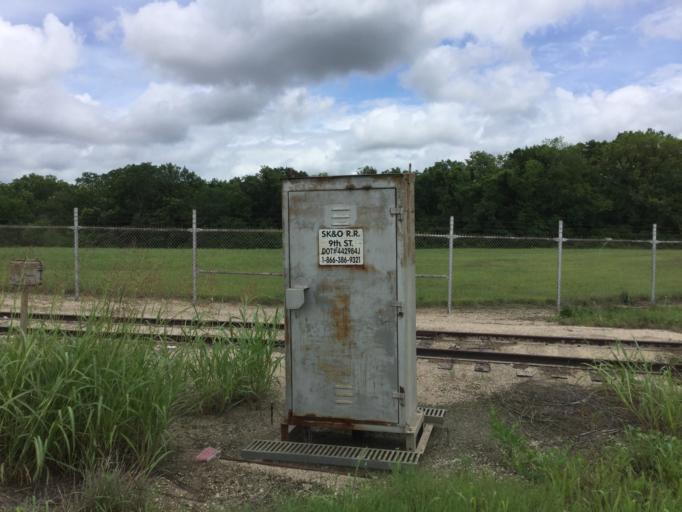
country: US
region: Kansas
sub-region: Allen County
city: Humboldt
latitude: 37.7910
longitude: -95.4352
